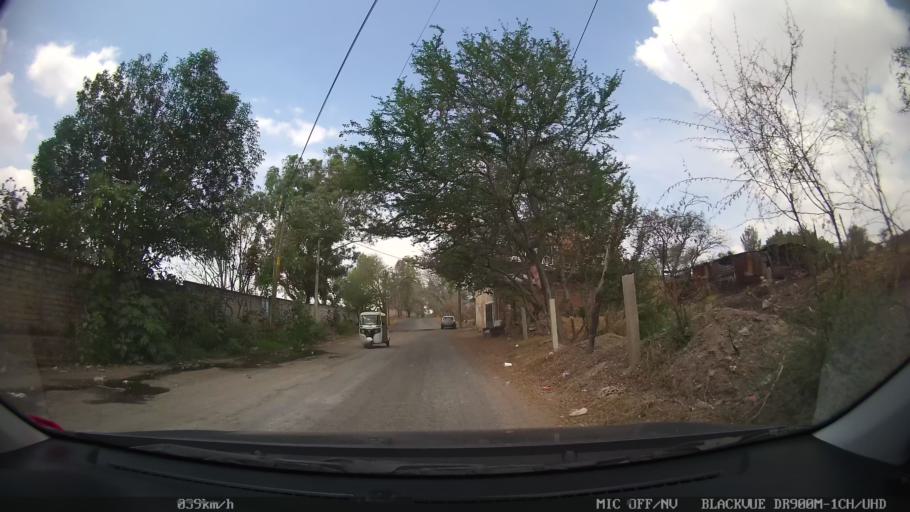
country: MX
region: Jalisco
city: Tonala
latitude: 20.6297
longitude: -103.2236
